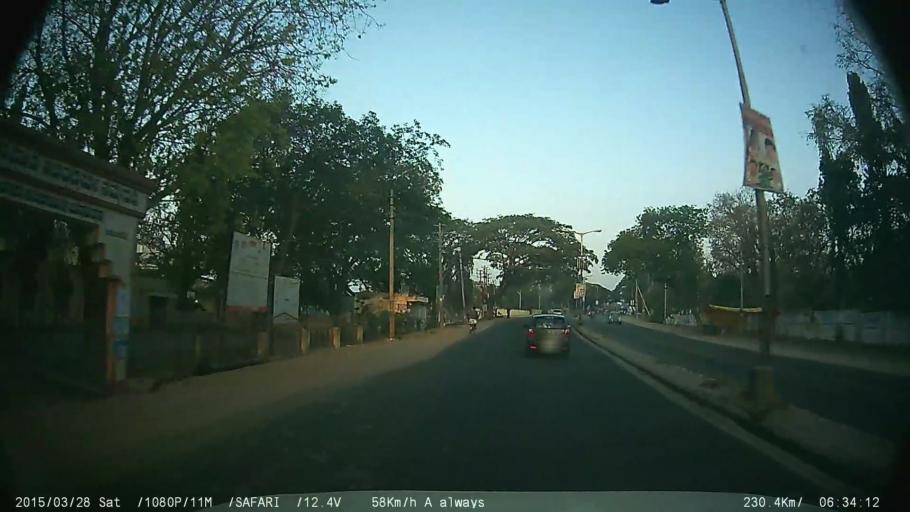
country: IN
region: Karnataka
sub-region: Ramanagara
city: Channapatna
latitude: 12.6518
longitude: 77.2074
